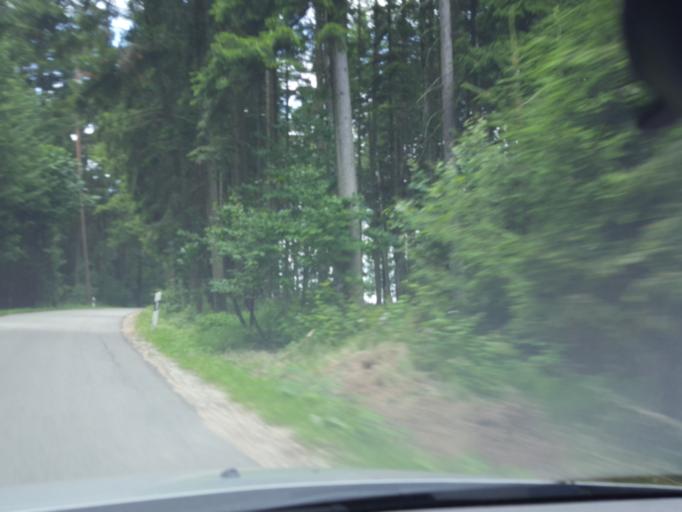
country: DE
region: Bavaria
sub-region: Upper Bavaria
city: Neumarkt-Sankt Veit
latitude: 48.3921
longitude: 12.4887
